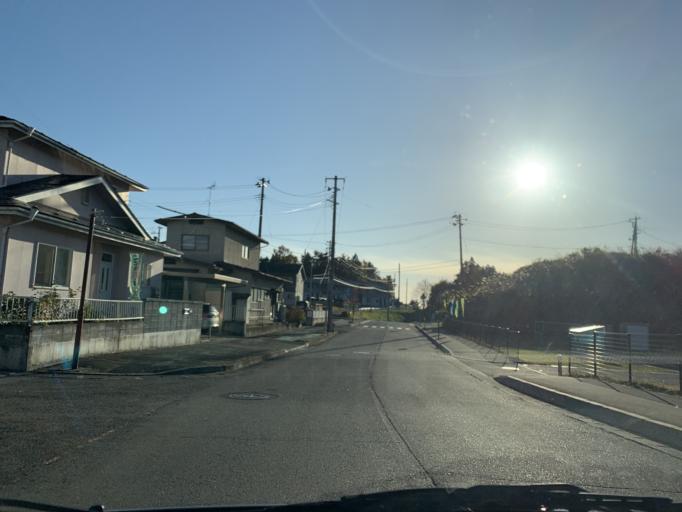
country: JP
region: Iwate
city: Mizusawa
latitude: 39.1903
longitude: 141.1910
